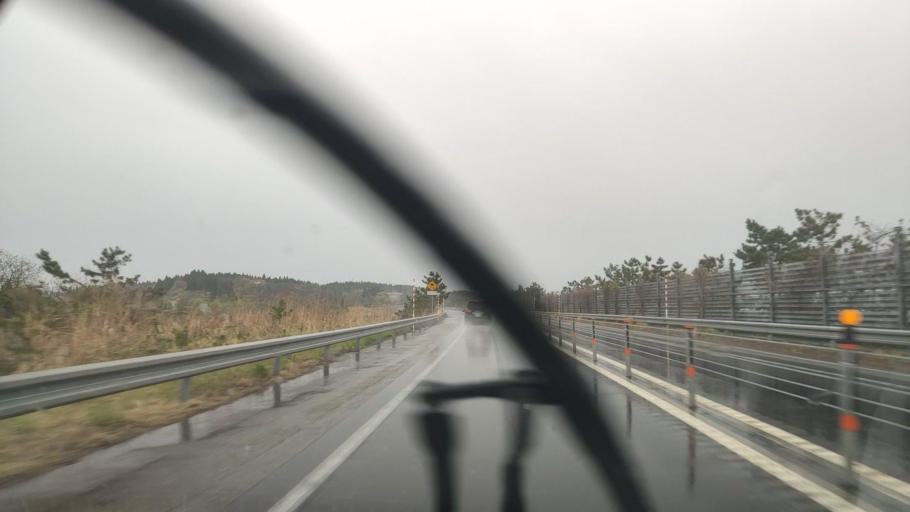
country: JP
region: Akita
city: Noshiromachi
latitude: 40.1797
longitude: 140.0616
